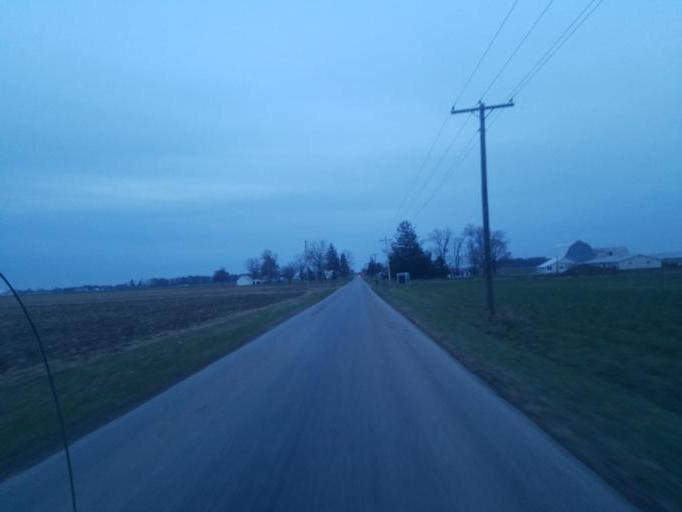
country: US
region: Indiana
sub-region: Adams County
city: Berne
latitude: 40.7305
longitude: -84.9650
